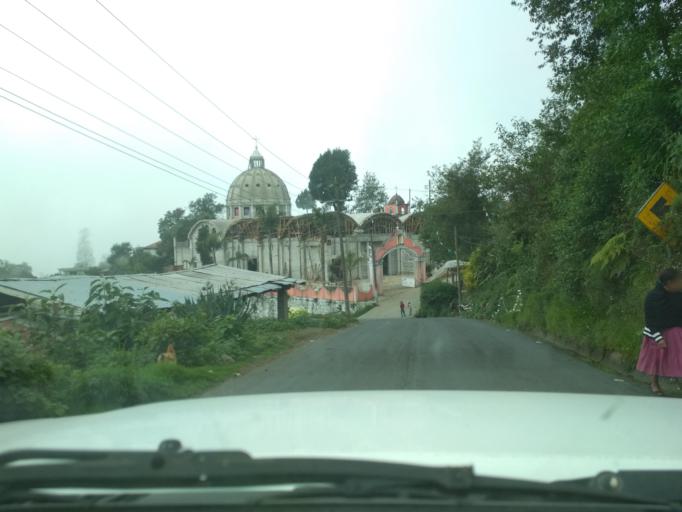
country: MX
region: Veracruz
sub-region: La Perla
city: Chilapa
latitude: 18.9657
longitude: -97.1687
